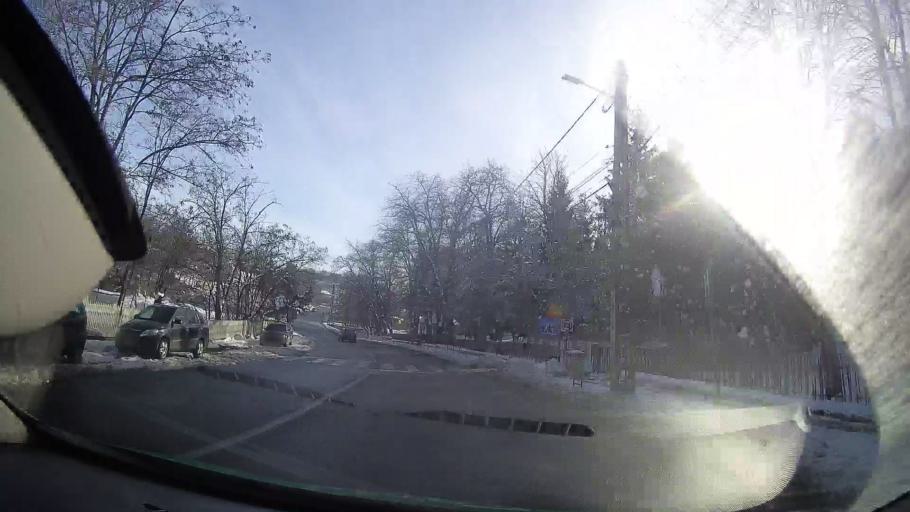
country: RO
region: Neamt
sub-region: Comuna Baltatesti
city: Baltatesti
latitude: 47.1203
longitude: 26.3097
